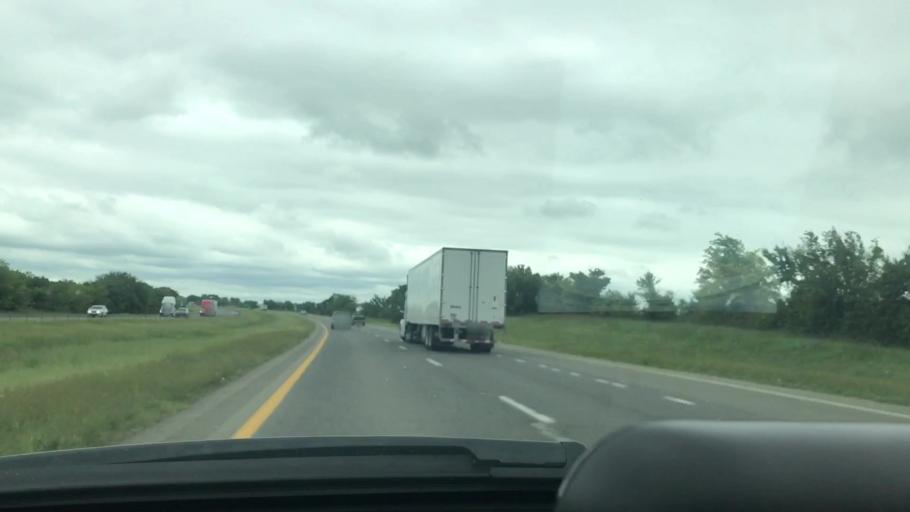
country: US
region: Oklahoma
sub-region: McIntosh County
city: Checotah
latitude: 35.4100
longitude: -95.5572
